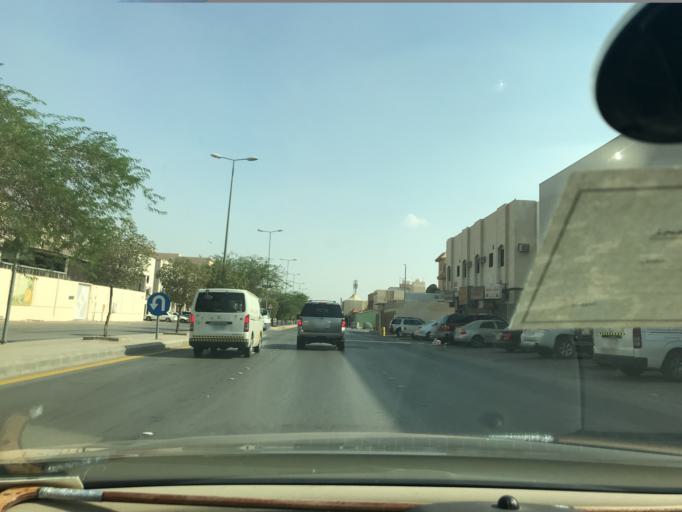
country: SA
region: Ar Riyad
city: Riyadh
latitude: 24.7464
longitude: 46.7631
